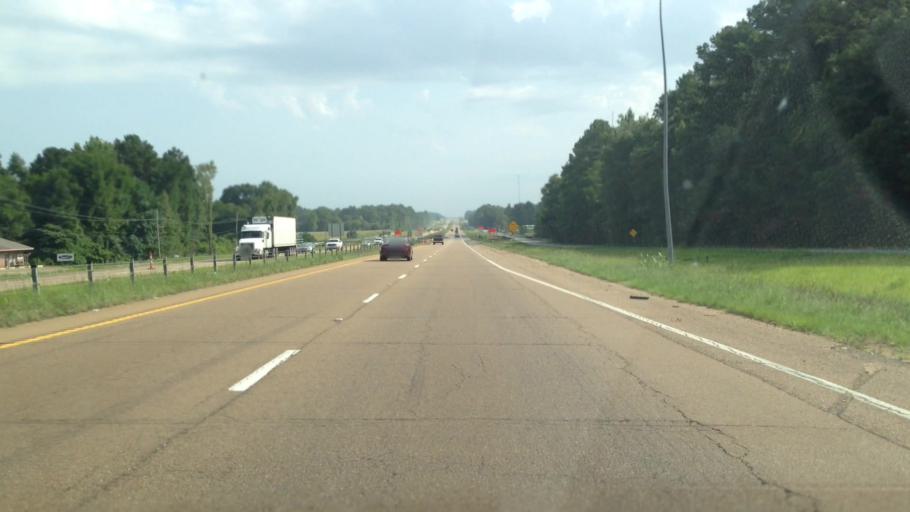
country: US
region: Mississippi
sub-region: Hinds County
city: Terry
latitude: 32.1058
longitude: -90.3003
